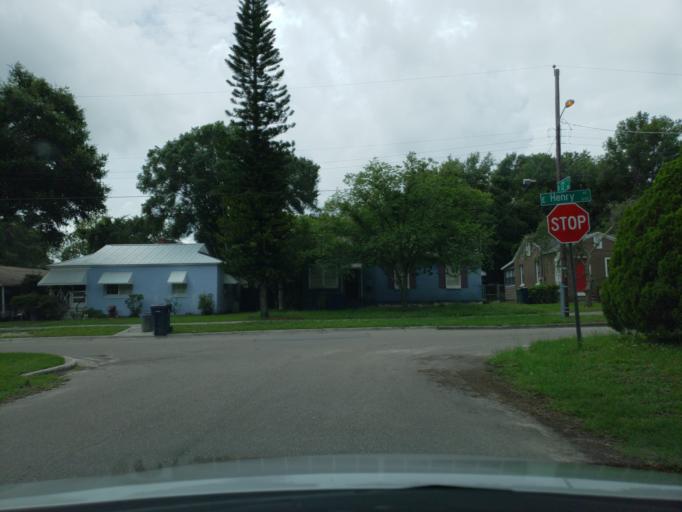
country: US
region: Florida
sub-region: Hillsborough County
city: Tampa
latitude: 27.9999
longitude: -82.4450
